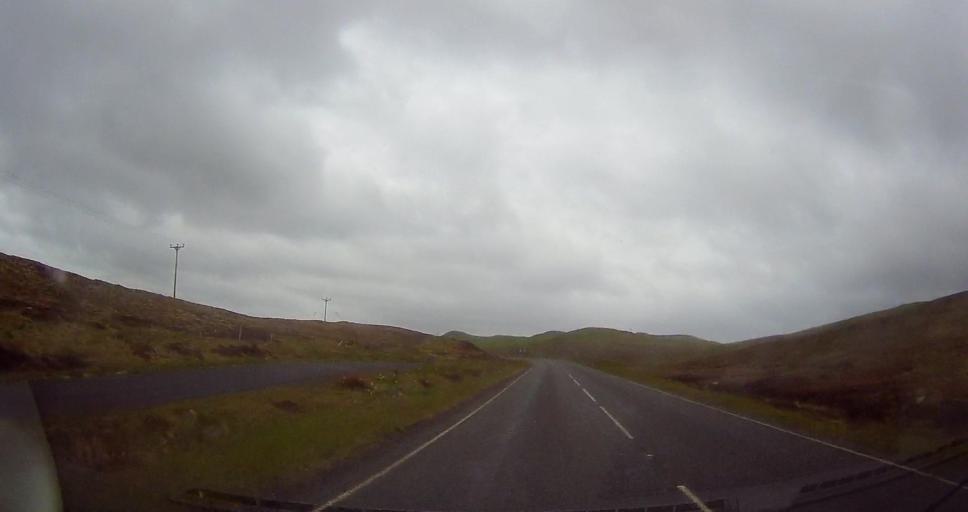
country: GB
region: Scotland
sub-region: Shetland Islands
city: Lerwick
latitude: 60.4360
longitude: -1.3974
